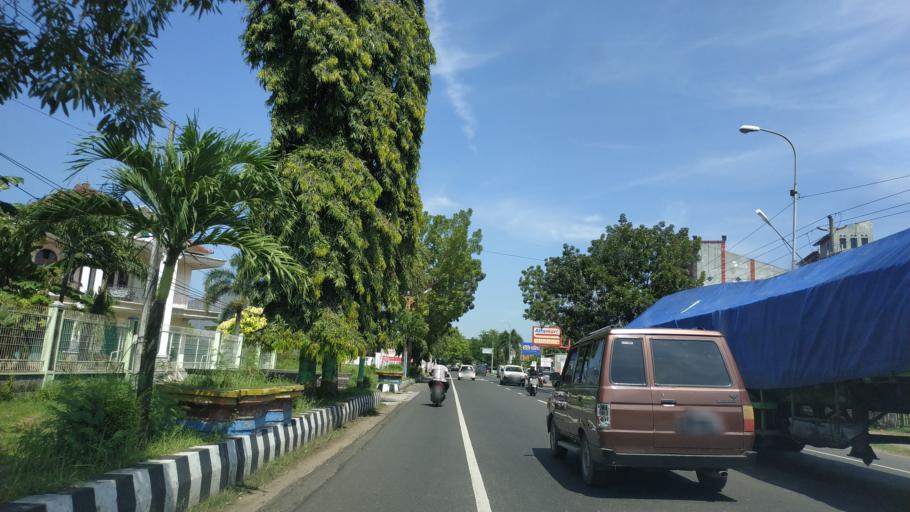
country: ID
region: Central Java
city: Baran
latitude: -6.7513
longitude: 111.0546
